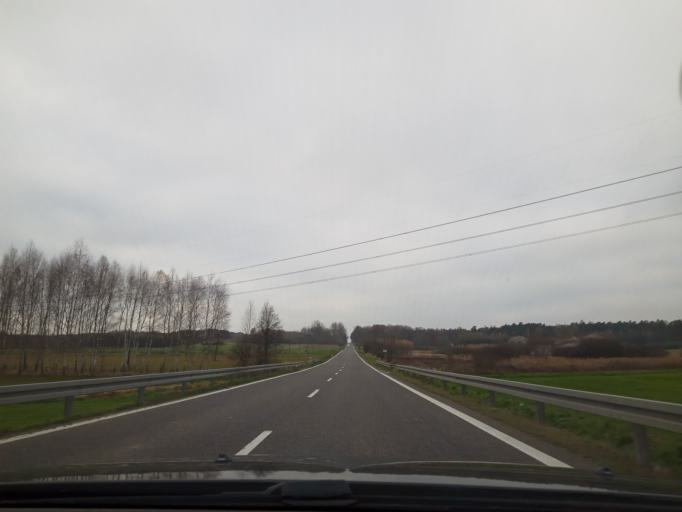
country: PL
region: Swietokrzyskie
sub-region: Powiat jedrzejowski
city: Imielno
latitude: 50.6091
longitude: 20.4806
